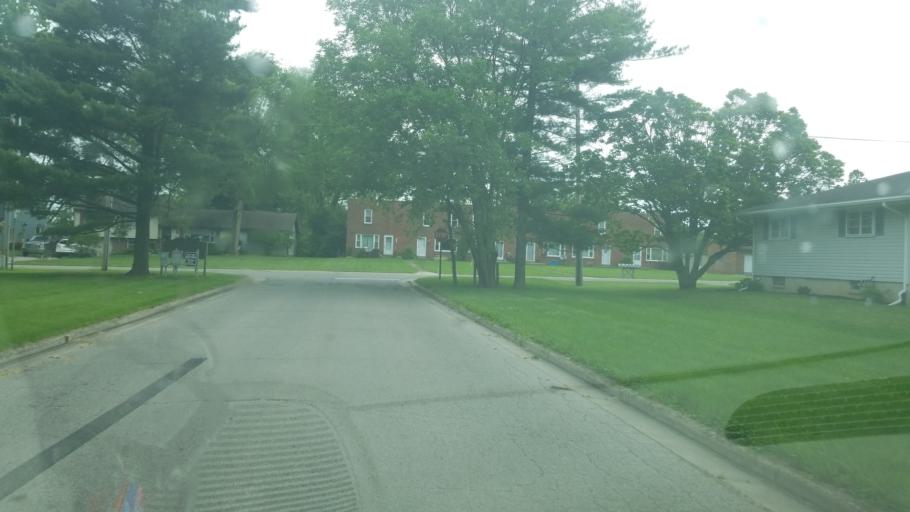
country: US
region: Ohio
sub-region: Crawford County
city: Bucyrus
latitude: 40.7897
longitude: -82.9822
